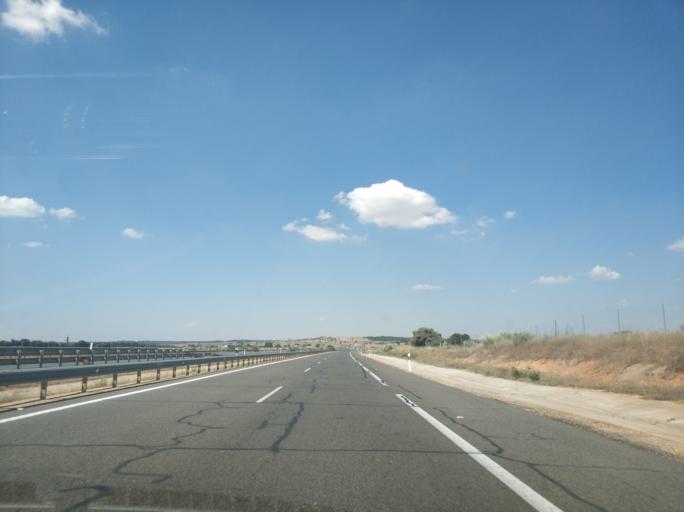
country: ES
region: Castille and Leon
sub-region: Provincia de Zamora
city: Cuelgamures
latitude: 41.2390
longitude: -5.7044
